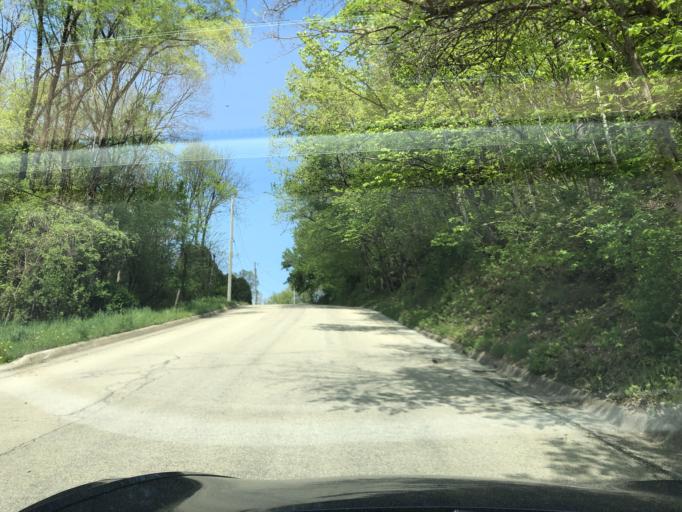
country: US
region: Iowa
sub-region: Dubuque County
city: Dubuque
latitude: 42.4822
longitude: -90.6688
